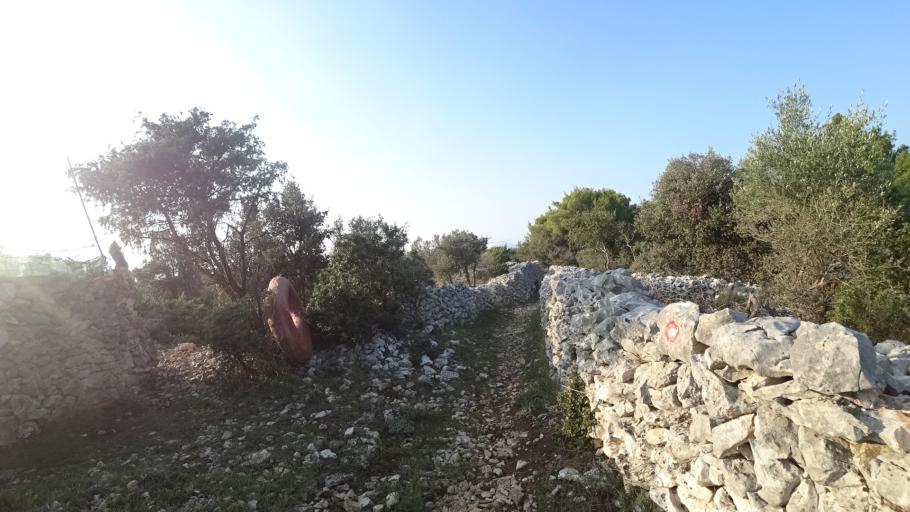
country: HR
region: Primorsko-Goranska
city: Mali Losinj
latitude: 44.5229
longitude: 14.4765
